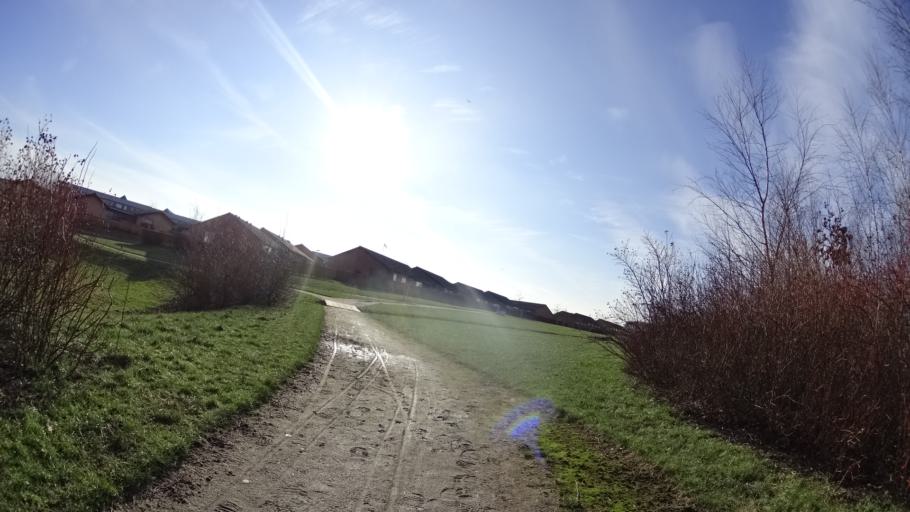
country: DK
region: Central Jutland
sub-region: Arhus Kommune
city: Stavtrup
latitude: 56.1149
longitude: 10.0986
